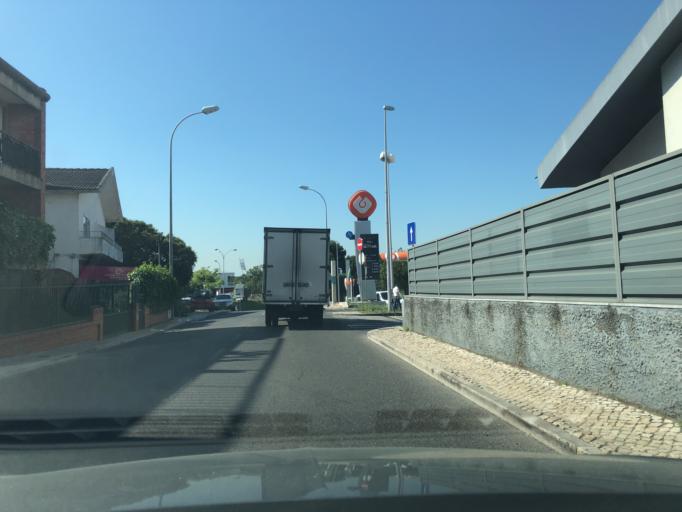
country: PT
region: Lisbon
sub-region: Oeiras
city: Quejas
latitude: 38.7164
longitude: -9.2633
